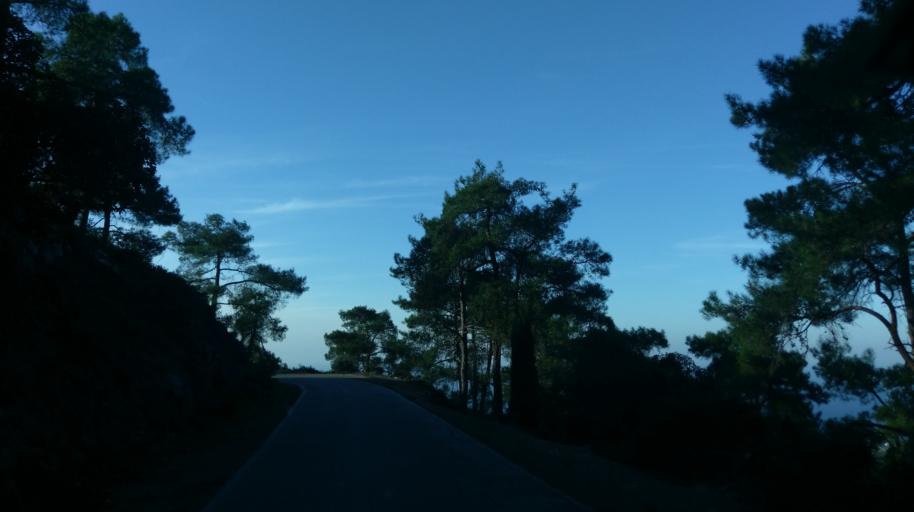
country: CY
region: Ammochostos
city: Lefkonoiko
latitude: 35.3059
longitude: 33.5719
